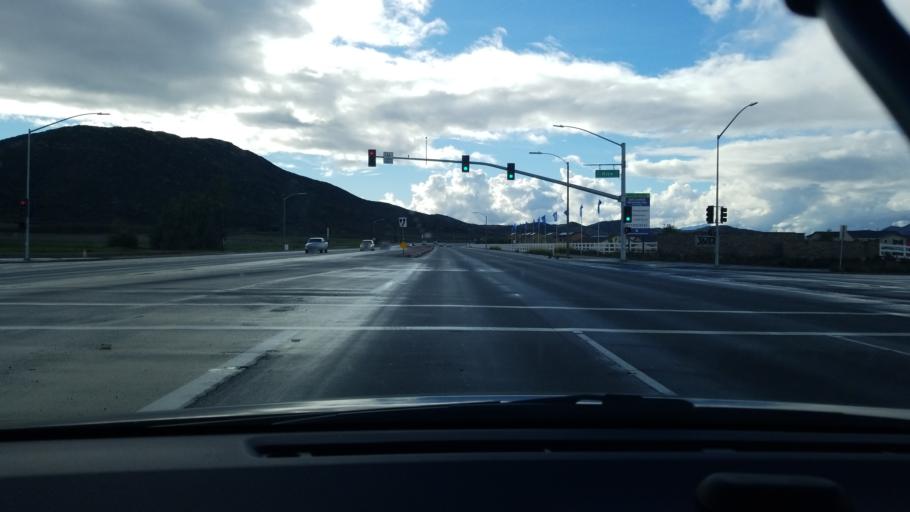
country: US
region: California
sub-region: Riverside County
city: Winchester
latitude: 33.6944
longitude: -117.0927
